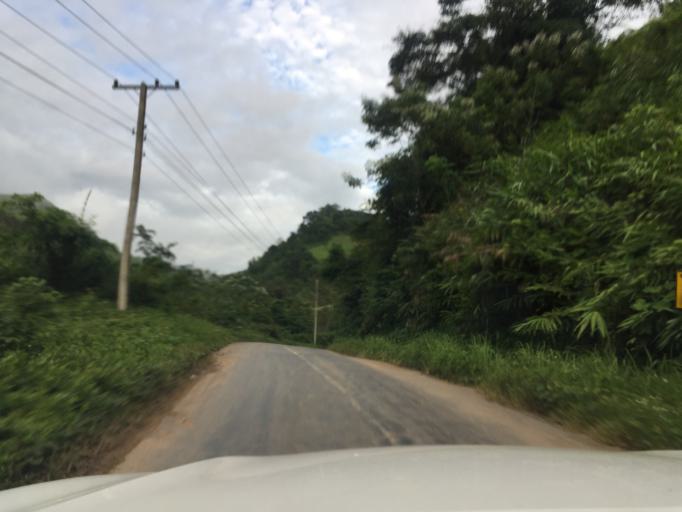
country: LA
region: Phongsali
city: Khoa
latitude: 21.1042
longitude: 102.2998
